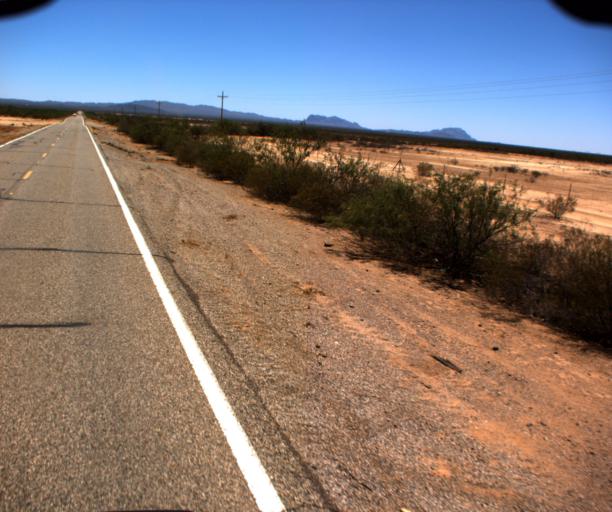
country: US
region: Arizona
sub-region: Pima County
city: Ajo
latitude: 32.1878
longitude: -112.3916
